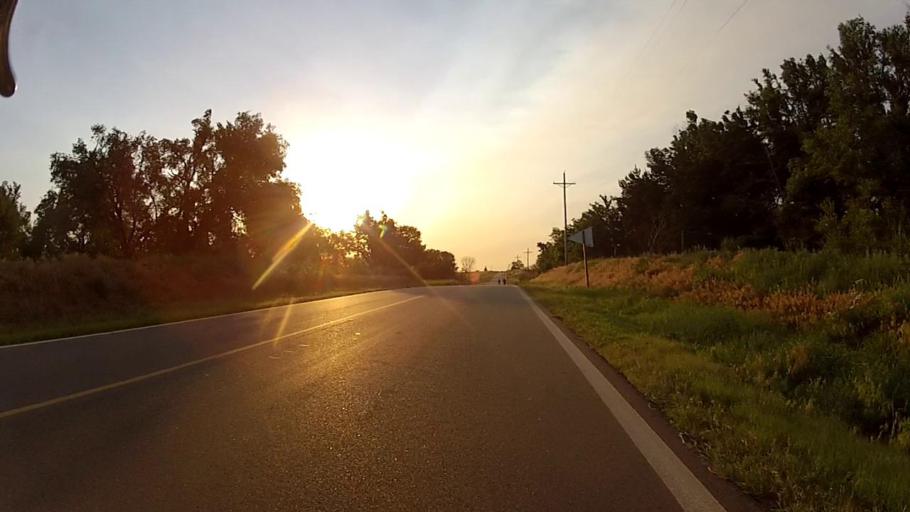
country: US
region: Kansas
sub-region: Harper County
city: Anthony
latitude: 37.1526
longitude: -97.9516
